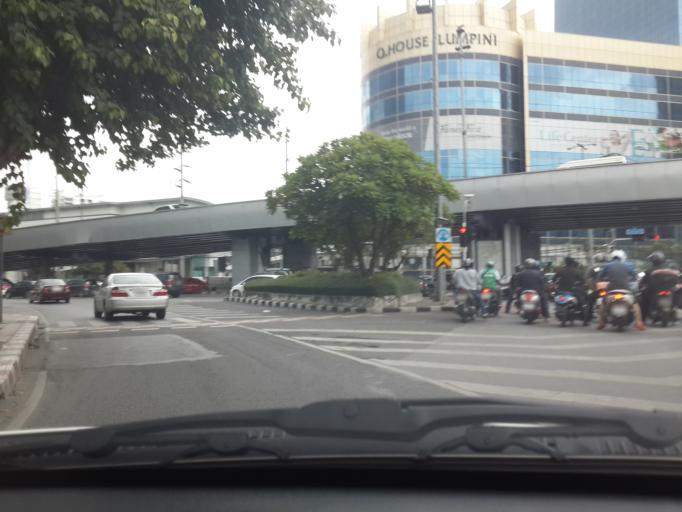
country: TH
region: Bangkok
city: Bang Rak
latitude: 13.7266
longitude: 100.5447
